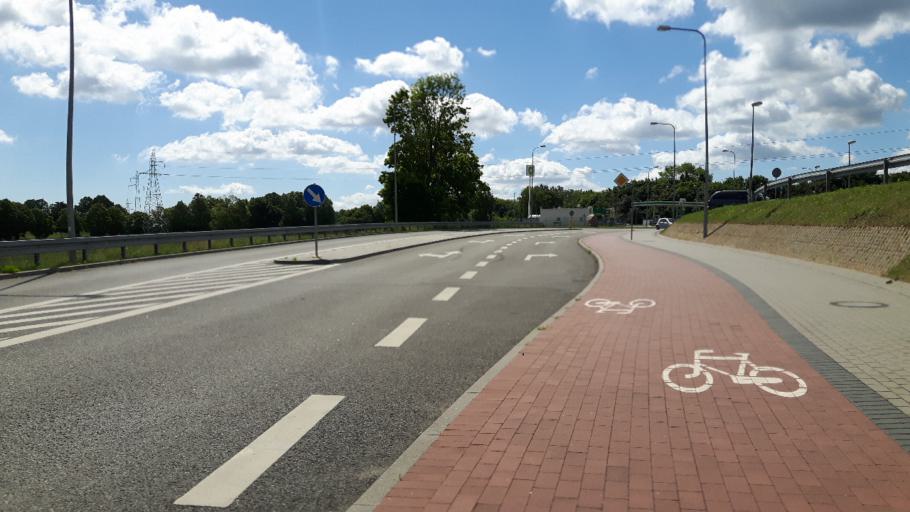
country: PL
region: Pomeranian Voivodeship
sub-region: Gdynia
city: Pogorze
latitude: 54.5655
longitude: 18.5056
